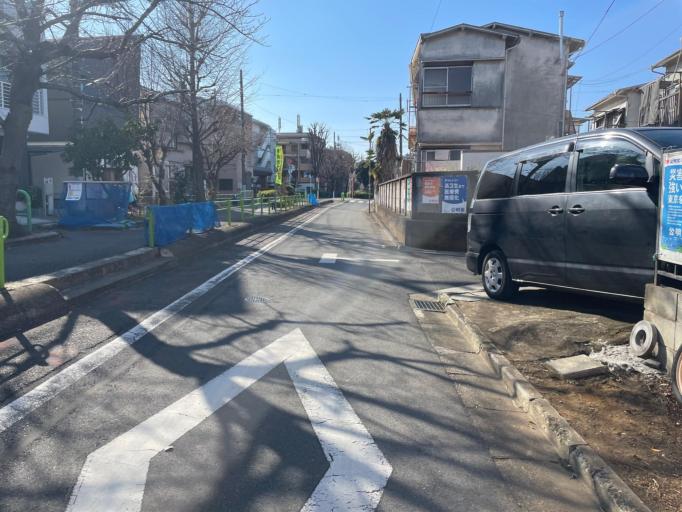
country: JP
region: Saitama
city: Wako
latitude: 35.7631
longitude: 139.6470
